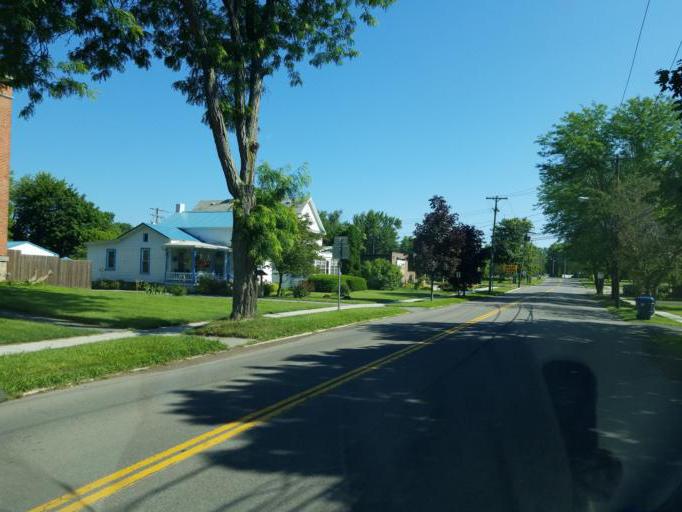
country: US
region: New York
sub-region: Wayne County
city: Clyde
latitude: 43.0869
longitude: -76.8679
